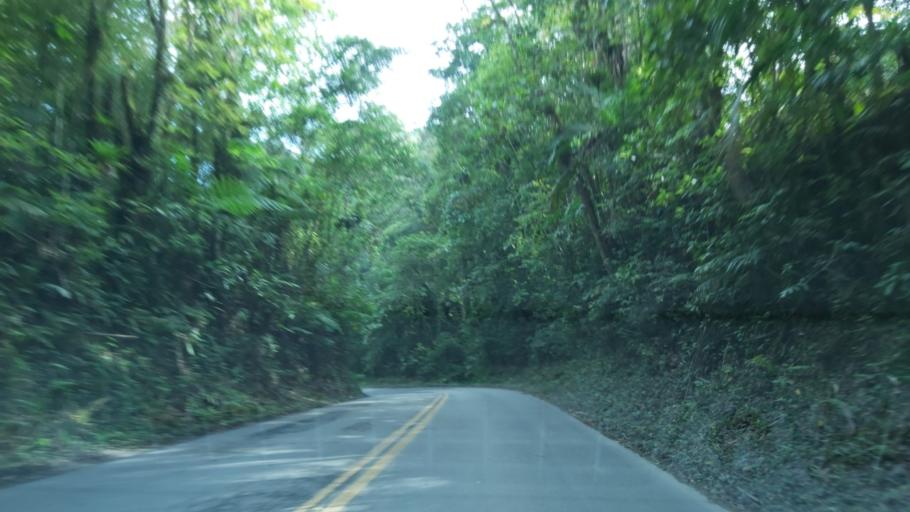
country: BR
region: Sao Paulo
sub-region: Juquia
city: Juquia
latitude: -24.0801
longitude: -47.6069
